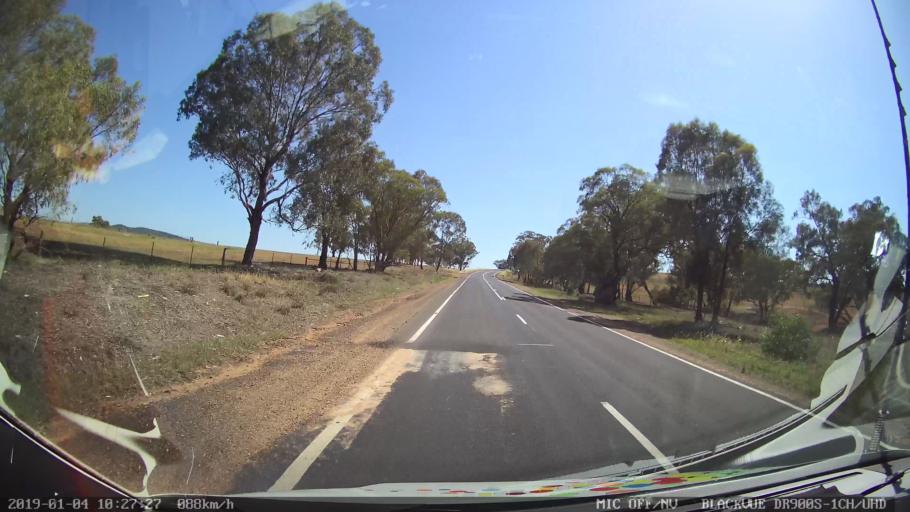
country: AU
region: New South Wales
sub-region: Cabonne
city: Canowindra
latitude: -33.3703
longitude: 148.5986
